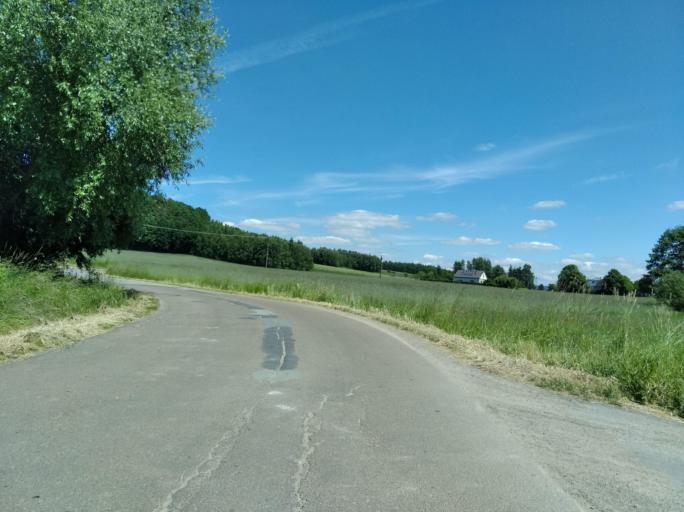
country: PL
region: Subcarpathian Voivodeship
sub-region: Powiat krosnienski
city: Wojaszowka
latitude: 49.7662
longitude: 21.6278
